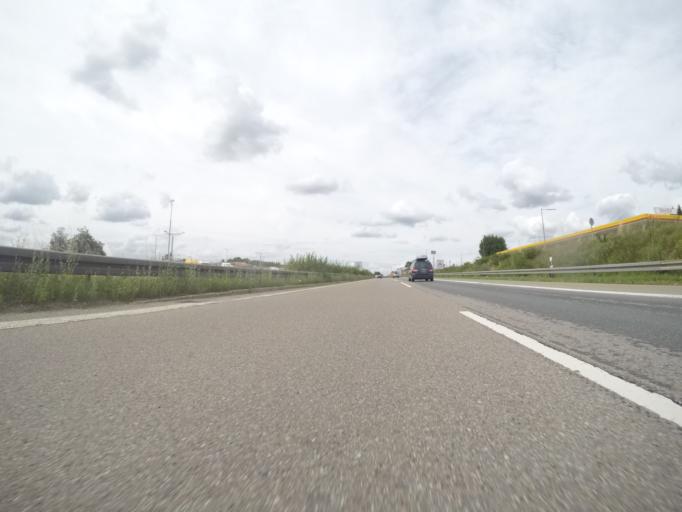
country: DE
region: Bavaria
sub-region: Upper Palatinate
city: Deining
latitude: 49.2696
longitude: 11.6020
